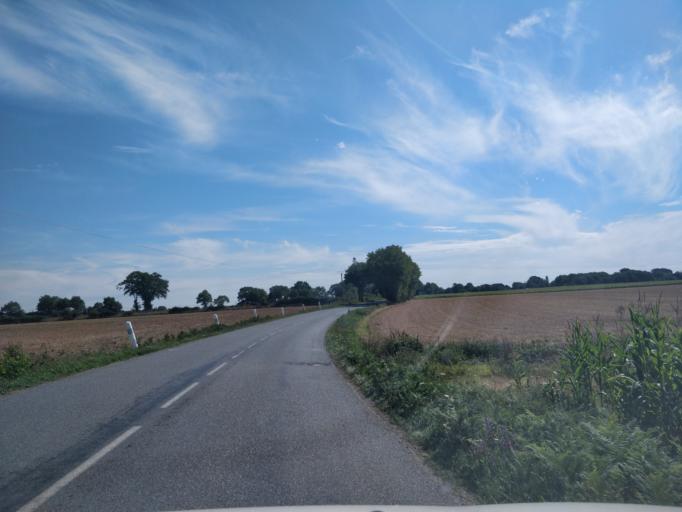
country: FR
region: Pays de la Loire
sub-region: Departement de la Loire-Atlantique
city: Derval
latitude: 47.6882
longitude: -1.6925
